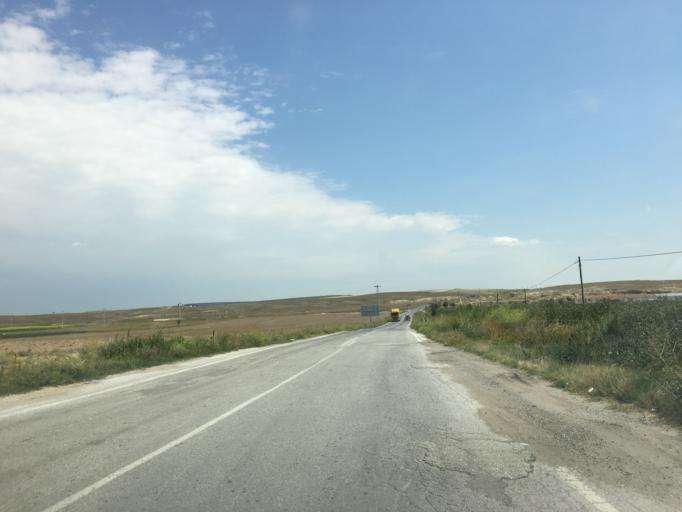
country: TR
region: Eskisehir
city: Cifteler
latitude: 39.3857
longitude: 31.0486
